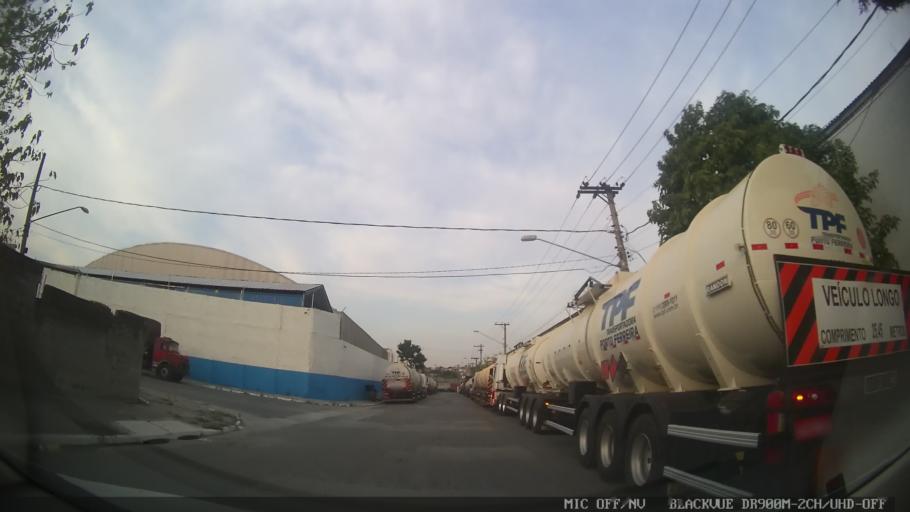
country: BR
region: Sao Paulo
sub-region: Sao Caetano Do Sul
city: Sao Caetano do Sul
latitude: -23.6000
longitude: -46.5868
